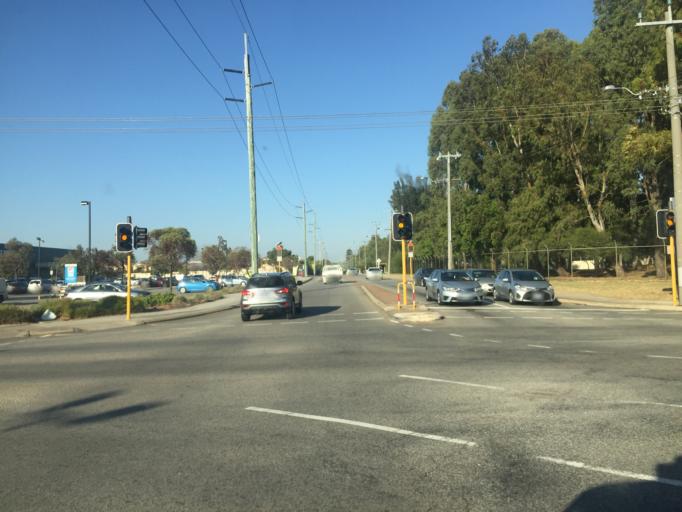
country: AU
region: Western Australia
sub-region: Belmont
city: Belmont
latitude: -31.9584
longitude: 115.9314
